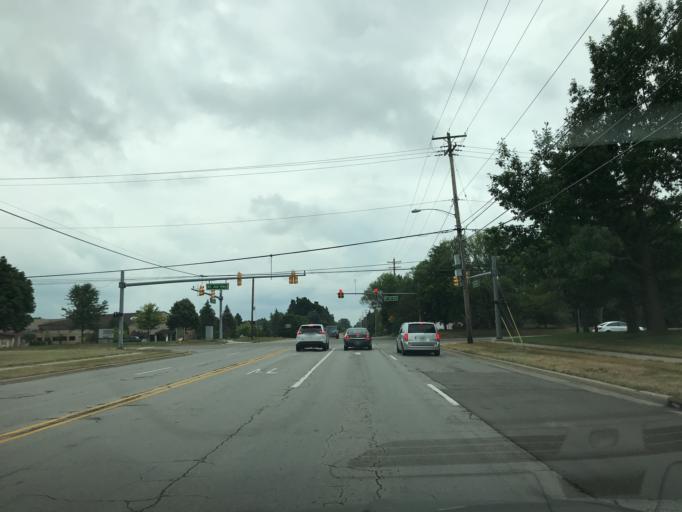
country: US
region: Michigan
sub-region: Eaton County
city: Waverly
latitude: 42.7271
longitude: -84.6621
